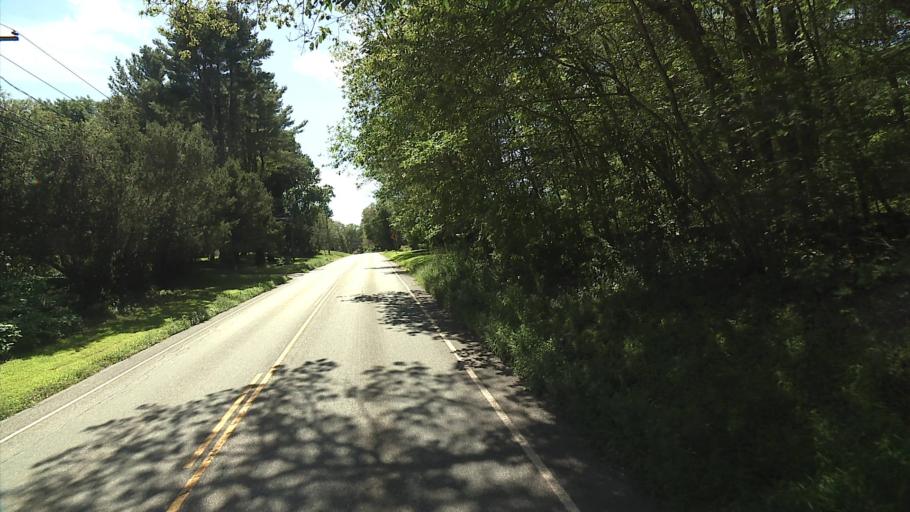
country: US
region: Connecticut
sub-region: Windham County
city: South Woodstock
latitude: 41.8514
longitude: -72.0118
